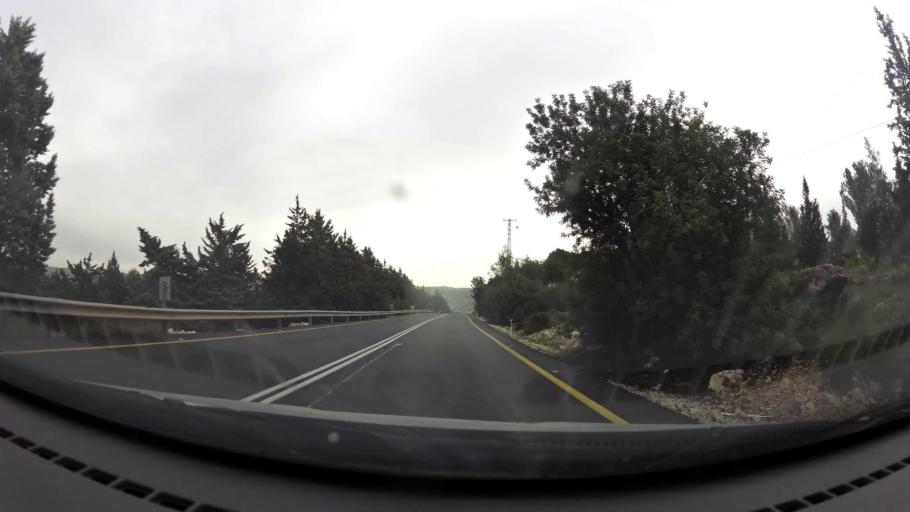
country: PS
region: West Bank
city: Surif
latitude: 31.6746
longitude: 35.0468
